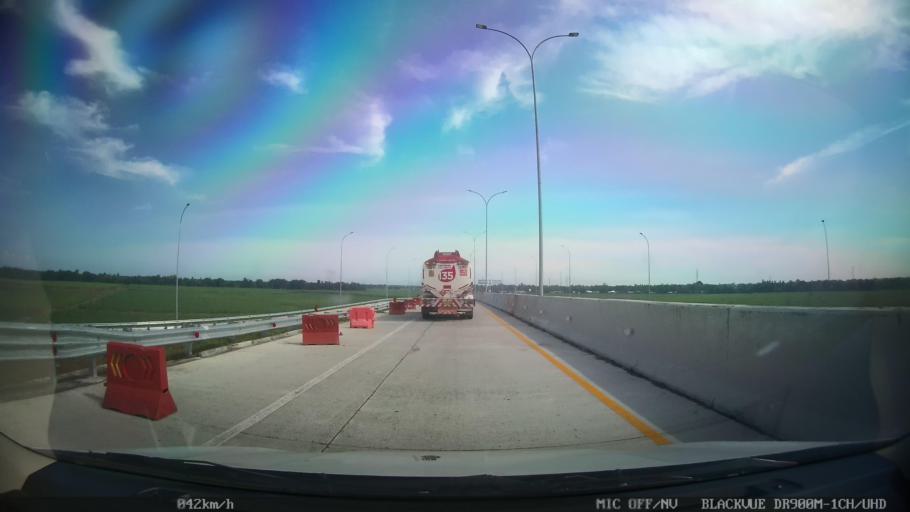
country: ID
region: North Sumatra
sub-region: Kabupaten Langkat
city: Stabat
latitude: 3.7134
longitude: 98.4937
